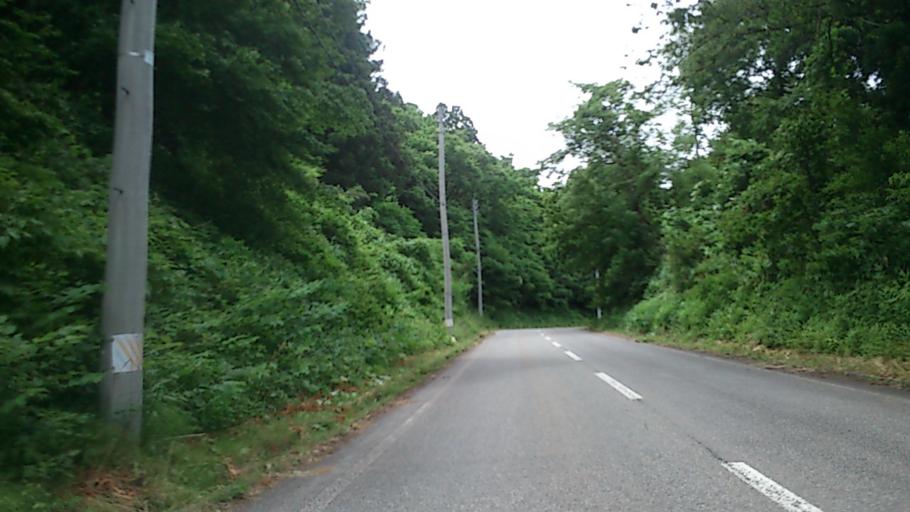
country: JP
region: Yamagata
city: Tsuruoka
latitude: 38.7867
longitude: 139.9784
